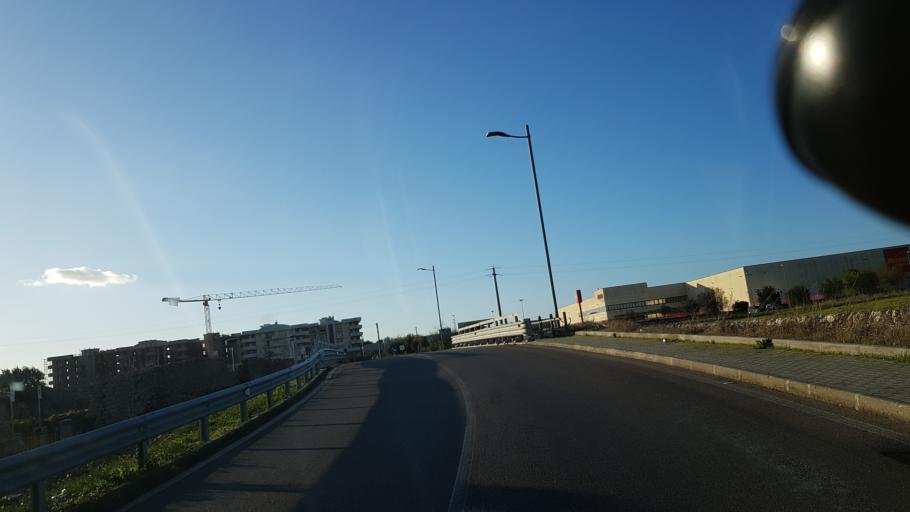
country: IT
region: Apulia
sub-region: Provincia di Bari
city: Gioia del Colle
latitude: 40.8017
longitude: 16.9085
